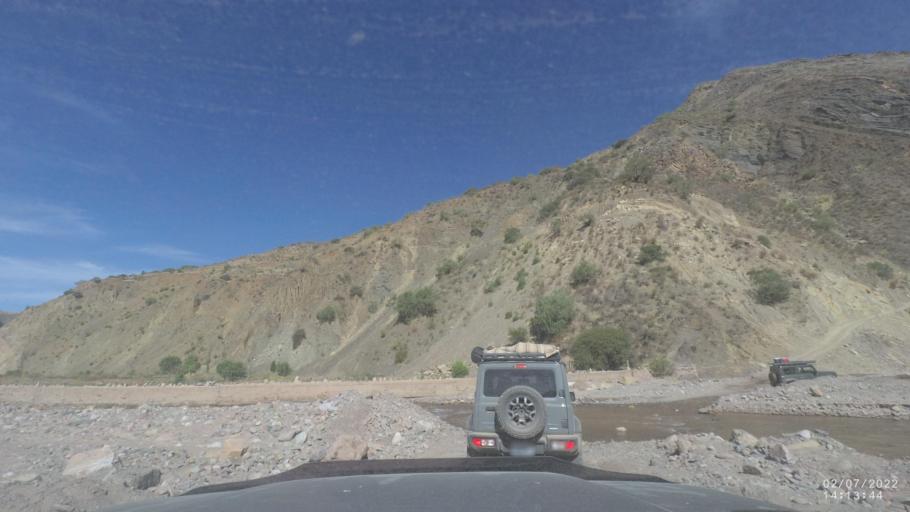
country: BO
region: Cochabamba
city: Irpa Irpa
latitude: -17.8254
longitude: -66.4034
